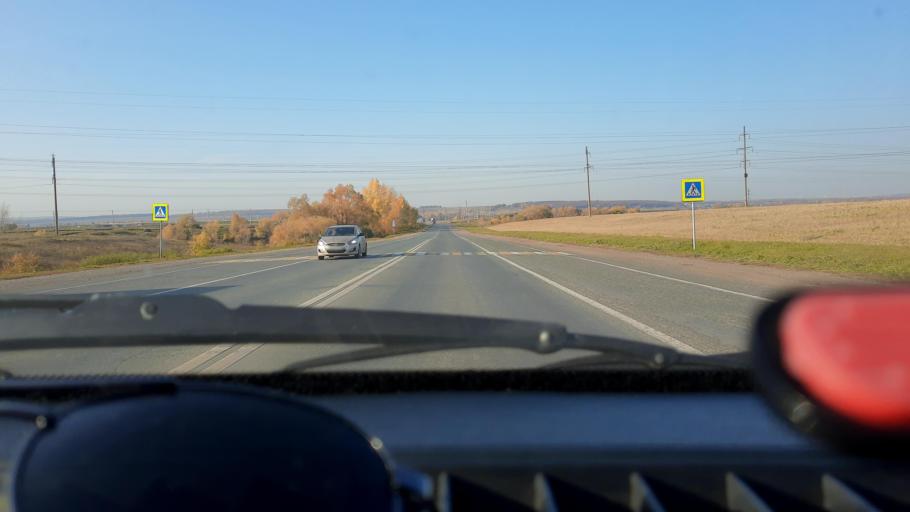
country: RU
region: Bashkortostan
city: Kabakovo
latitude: 54.4851
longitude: 55.9211
